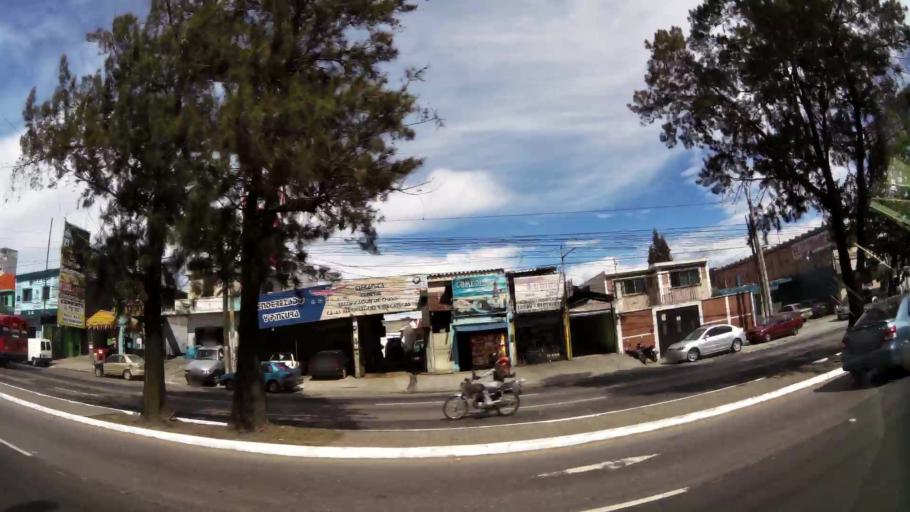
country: GT
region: Guatemala
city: Mixco
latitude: 14.6354
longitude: -90.5613
